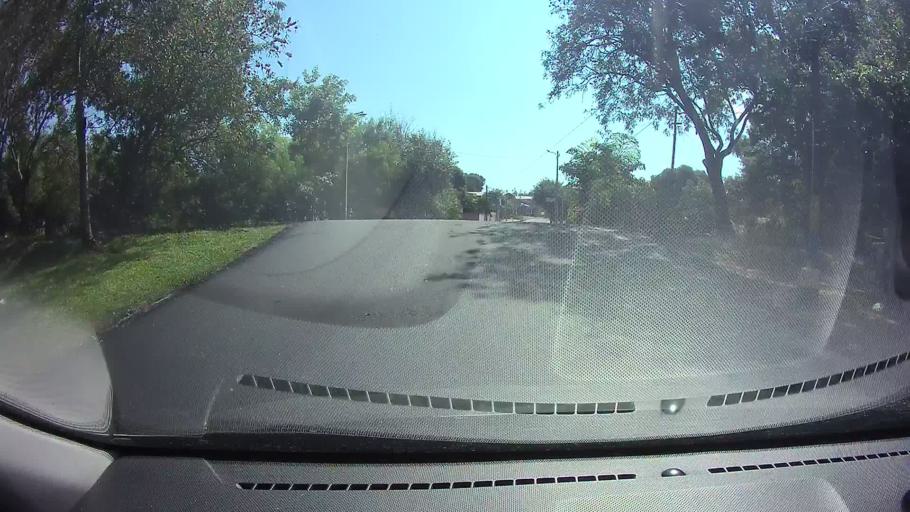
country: PY
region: Central
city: San Lorenzo
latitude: -25.2638
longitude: -57.4873
